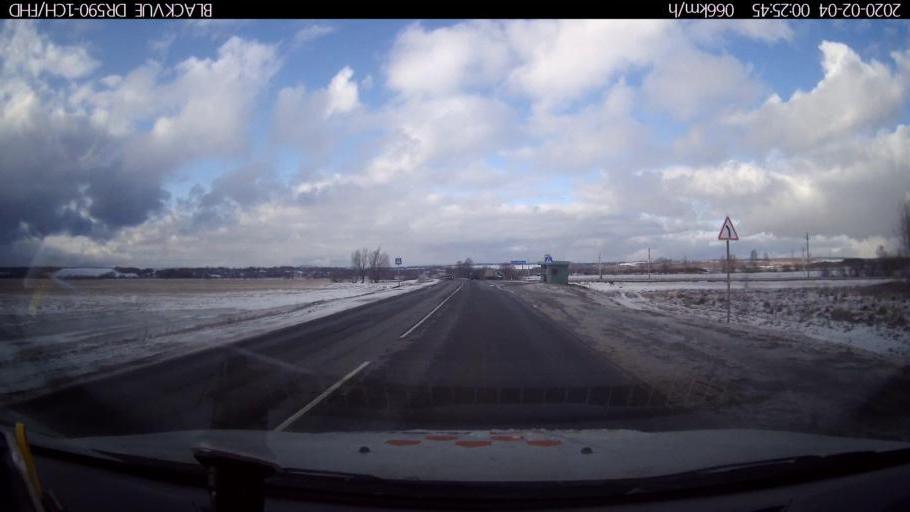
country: RU
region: Nizjnij Novgorod
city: Kstovo
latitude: 56.0087
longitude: 44.2078
